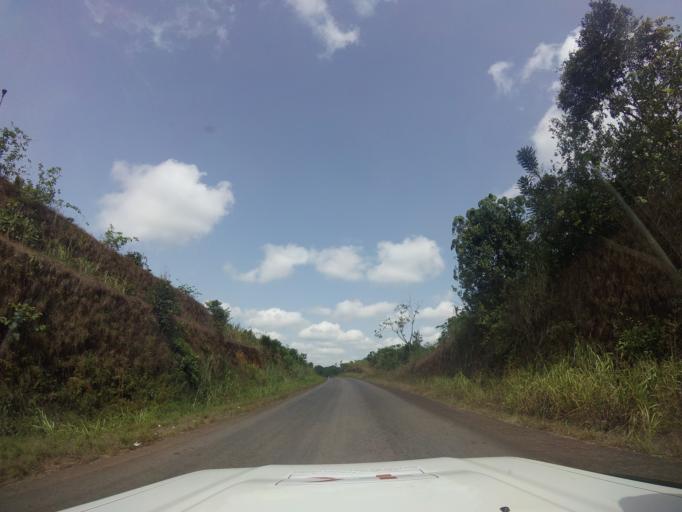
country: LR
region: Bomi
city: Tubmanburg
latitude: 6.7318
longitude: -10.9939
